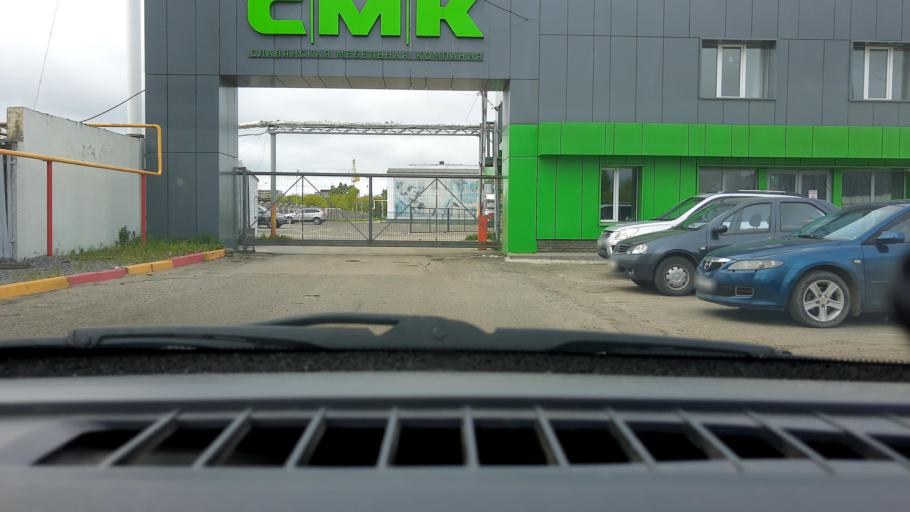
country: RU
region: Nizjnij Novgorod
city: Gorbatovka
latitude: 56.3515
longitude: 43.8223
